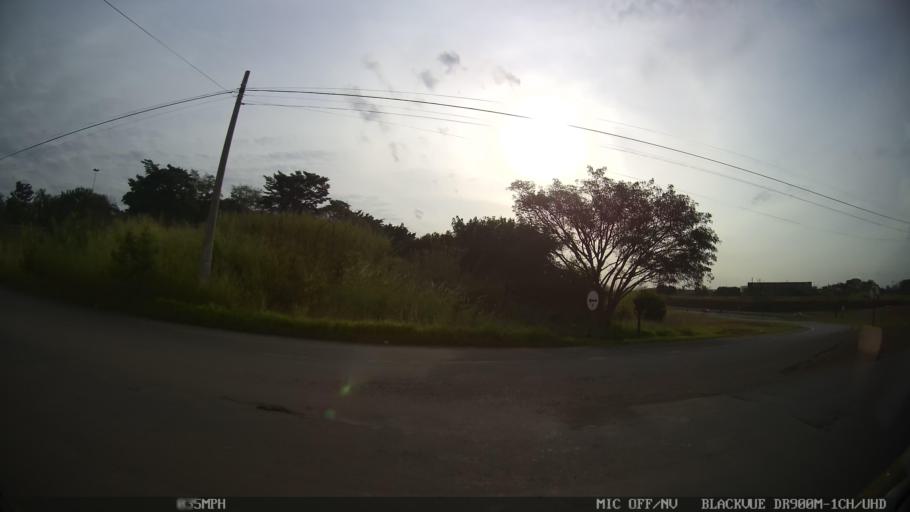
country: BR
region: Sao Paulo
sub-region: Piracicaba
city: Piracicaba
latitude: -22.7259
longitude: -47.5854
